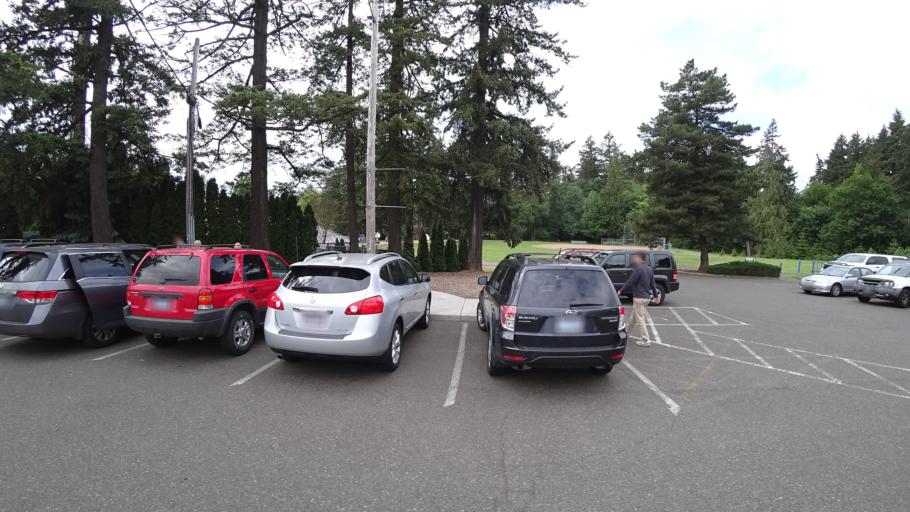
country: US
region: Oregon
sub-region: Washington County
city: Garden Home-Whitford
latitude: 45.4669
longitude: -122.7525
